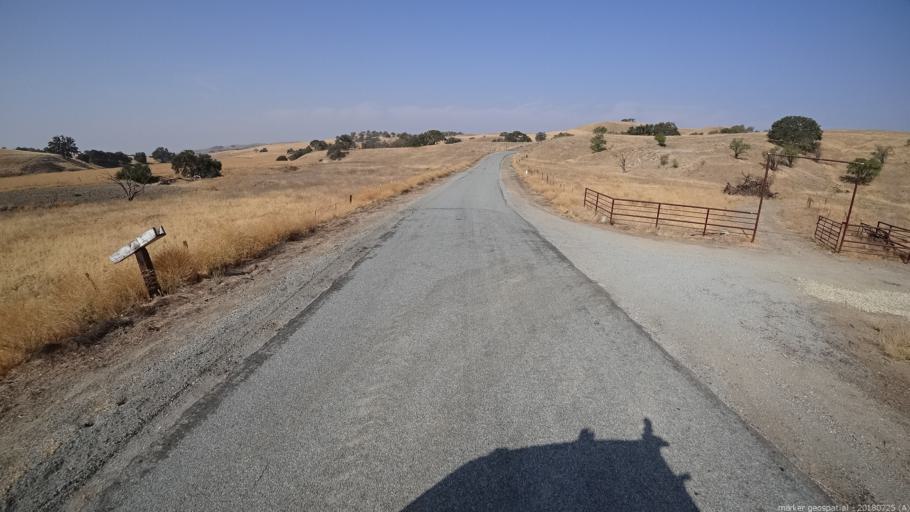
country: US
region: California
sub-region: San Luis Obispo County
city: San Miguel
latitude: 35.8062
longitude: -120.5334
